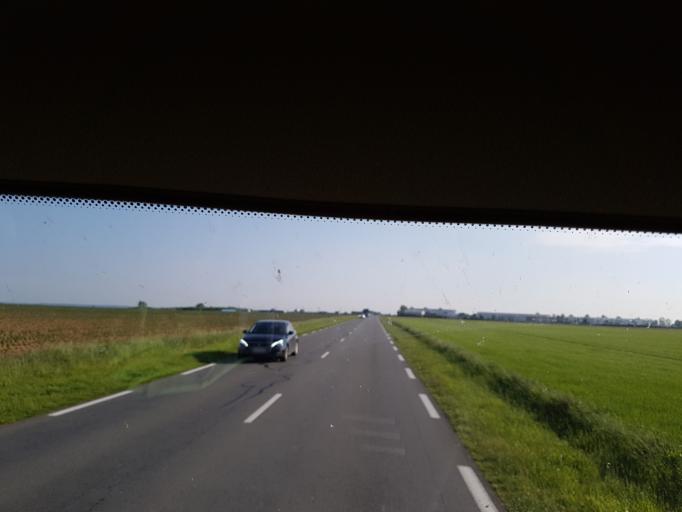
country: FR
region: Picardie
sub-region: Departement de la Somme
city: Abbeville
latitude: 50.1416
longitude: 1.8437
